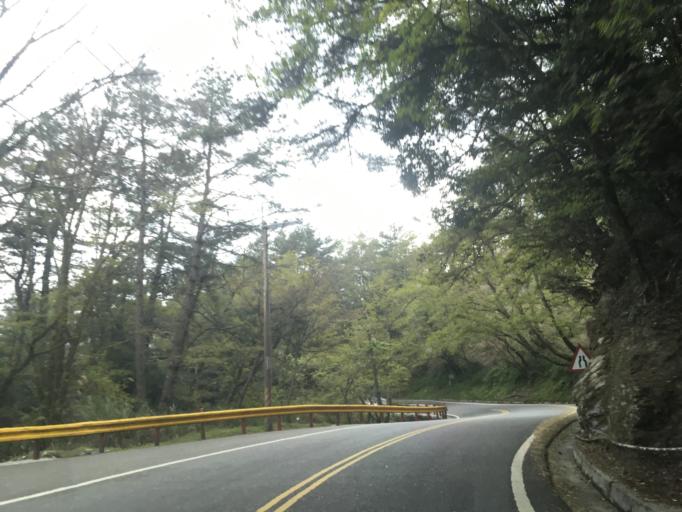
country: TW
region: Taiwan
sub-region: Hualien
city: Hualian
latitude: 24.1816
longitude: 121.3232
